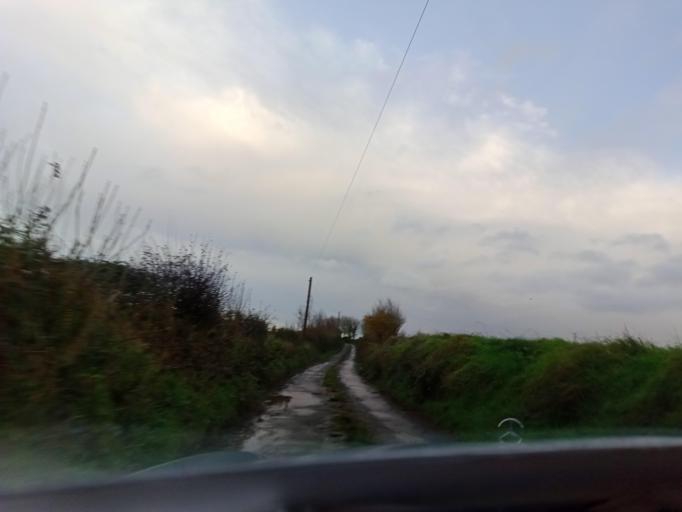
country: IE
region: Leinster
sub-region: Loch Garman
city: New Ross
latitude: 52.3459
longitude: -7.0203
